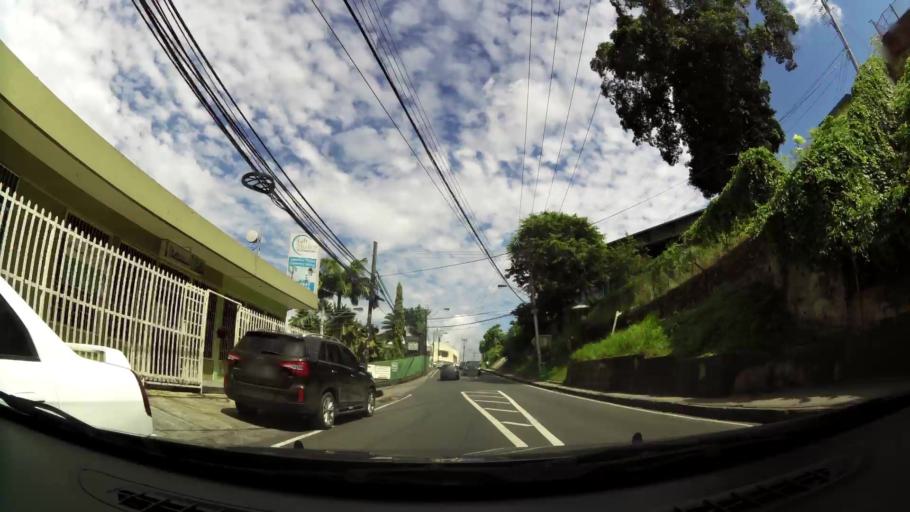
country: TT
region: City of San Fernando
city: San Fernando
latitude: 10.2820
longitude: -61.4624
